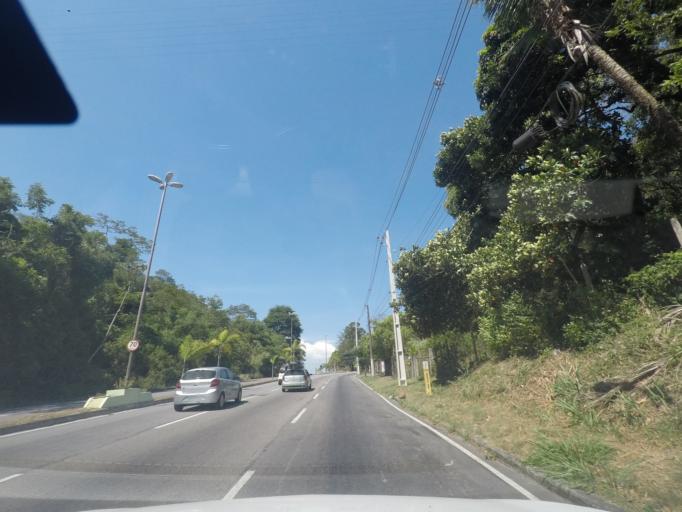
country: BR
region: Rio de Janeiro
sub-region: Niteroi
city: Niteroi
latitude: -22.9220
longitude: -43.0554
